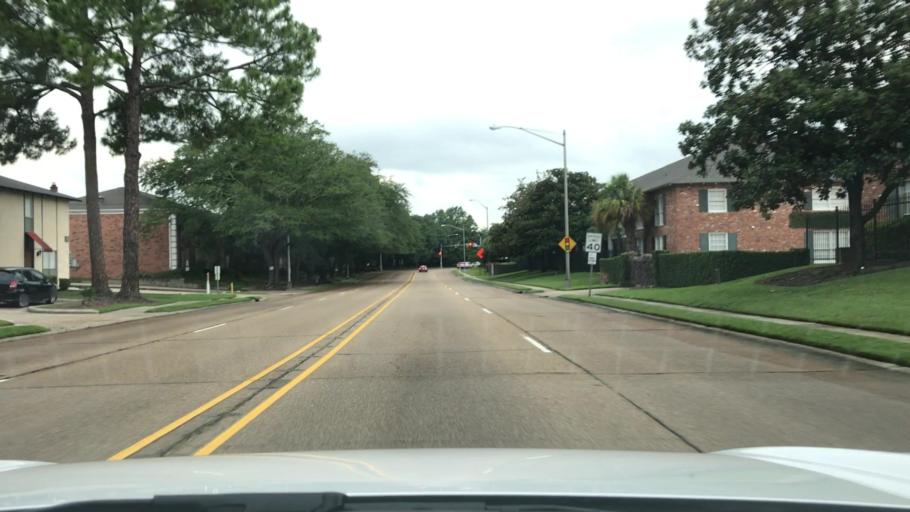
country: US
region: Louisiana
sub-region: East Baton Rouge Parish
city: Baton Rouge
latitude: 30.4402
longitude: -91.1361
